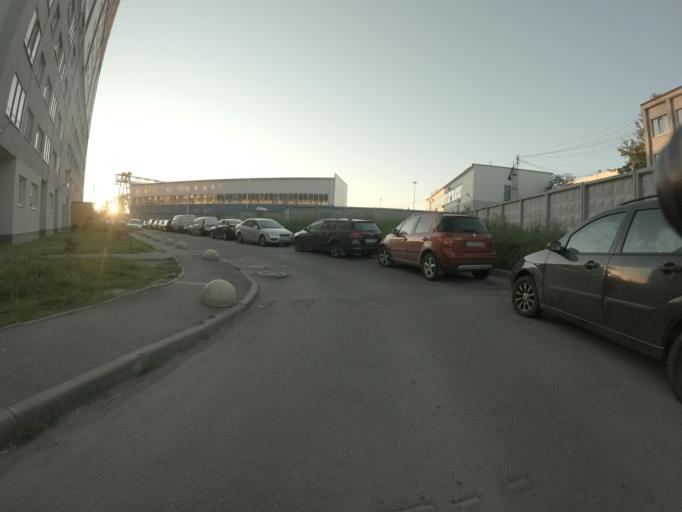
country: RU
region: St.-Petersburg
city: Krasnogvargeisky
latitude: 59.9789
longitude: 30.5146
